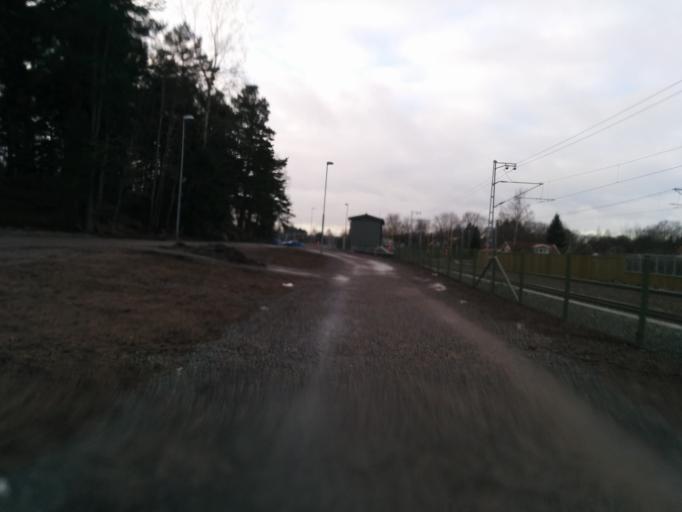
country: SE
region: Stockholm
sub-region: Vallentuna Kommun
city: Vallentuna
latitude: 59.4914
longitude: 18.0646
